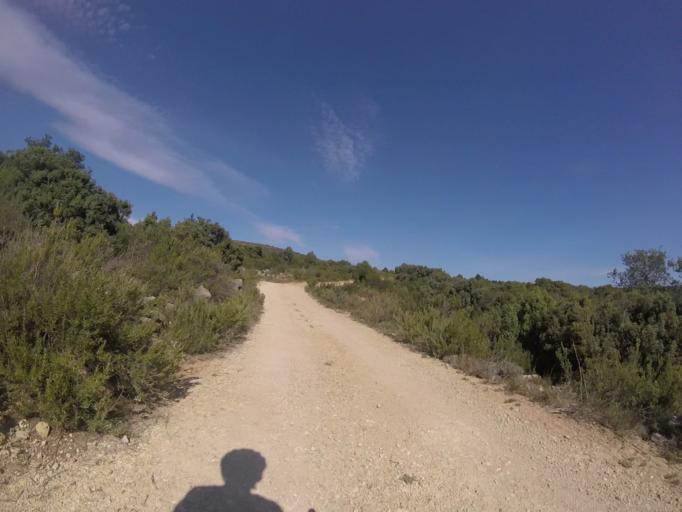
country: ES
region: Valencia
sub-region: Provincia de Castello
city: Sierra-Engarceran
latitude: 40.2705
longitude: 0.0153
